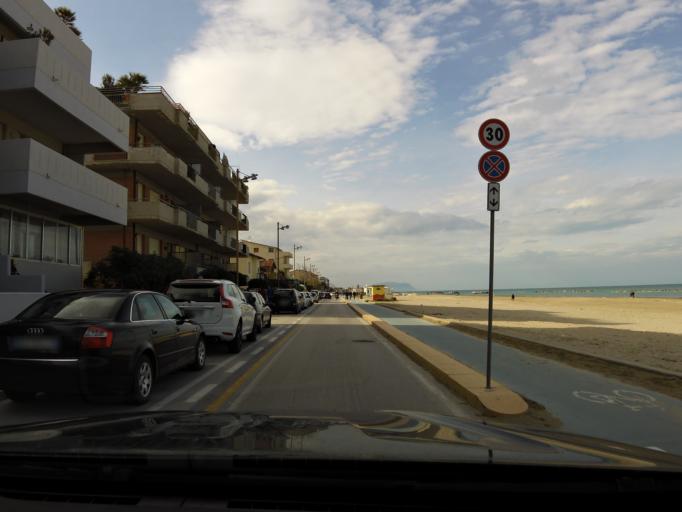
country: IT
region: The Marches
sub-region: Provincia di Macerata
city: Civitanova Marche
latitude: 43.3242
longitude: 13.7177
